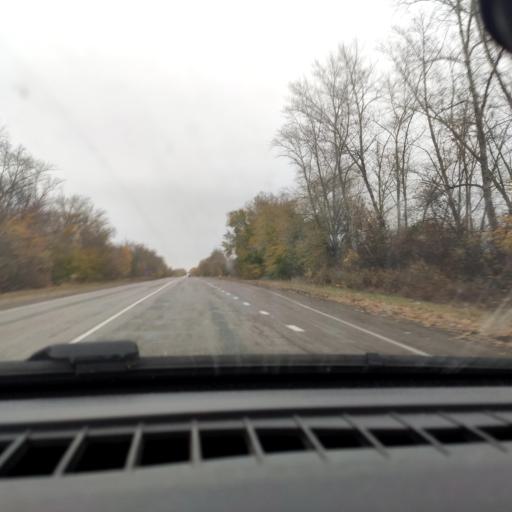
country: RU
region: Voronezj
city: Uryv-Pokrovka
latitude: 51.1457
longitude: 39.0584
